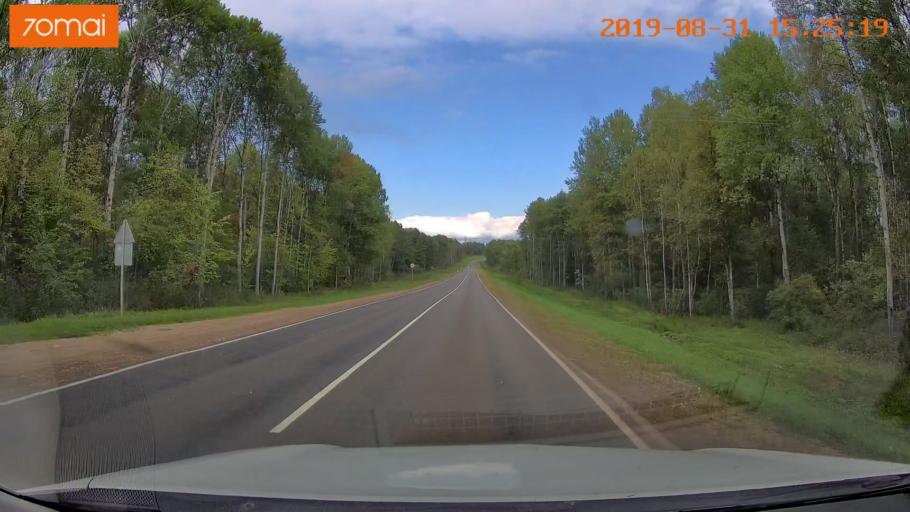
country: RU
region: Kaluga
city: Baryatino
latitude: 54.5398
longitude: 34.5180
